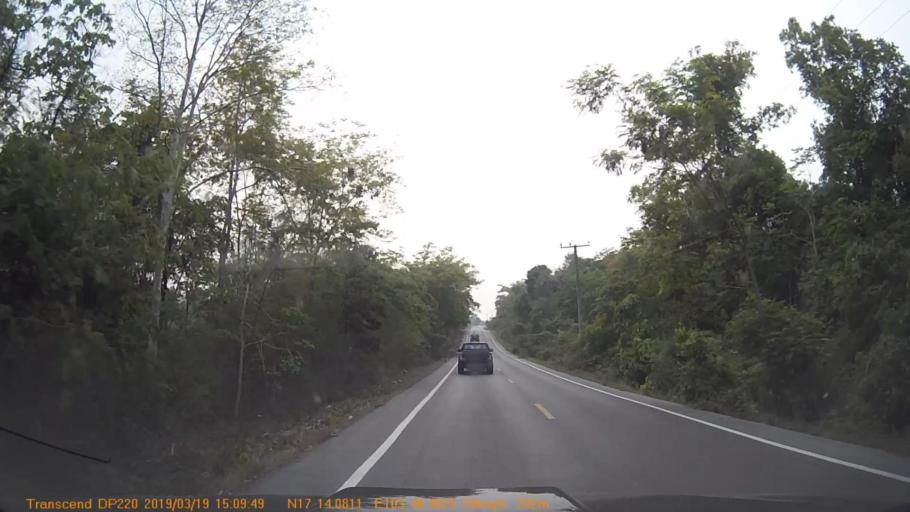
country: TH
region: Sakon Nakhon
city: Nikhom Nam Un
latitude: 17.2348
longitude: 103.7732
